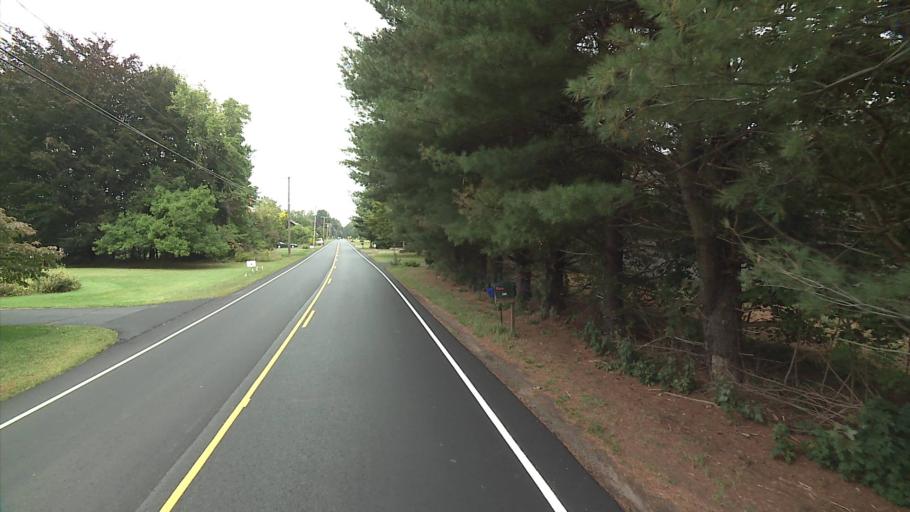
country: US
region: Connecticut
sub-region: Hartford County
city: Suffield Depot
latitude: 42.0134
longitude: -72.6921
